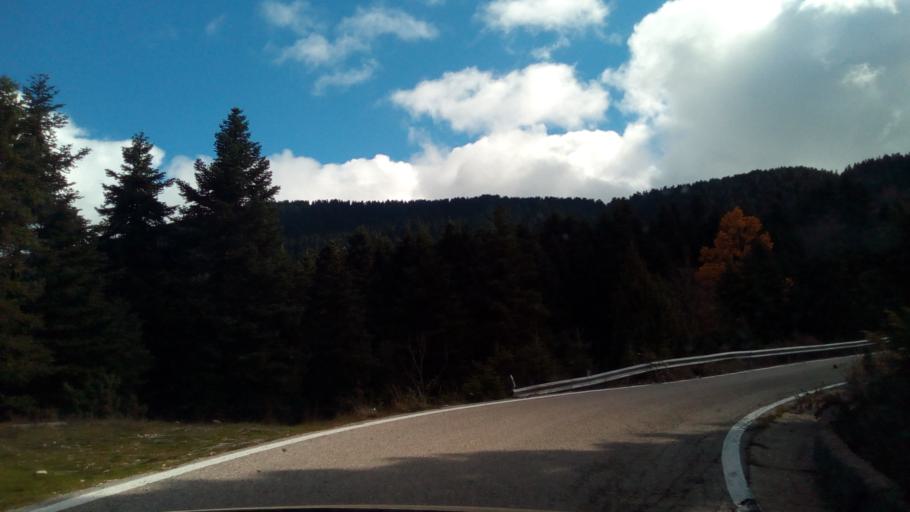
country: GR
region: West Greece
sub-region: Nomos Aitolias kai Akarnanias
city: Nafpaktos
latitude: 38.5852
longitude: 21.9376
